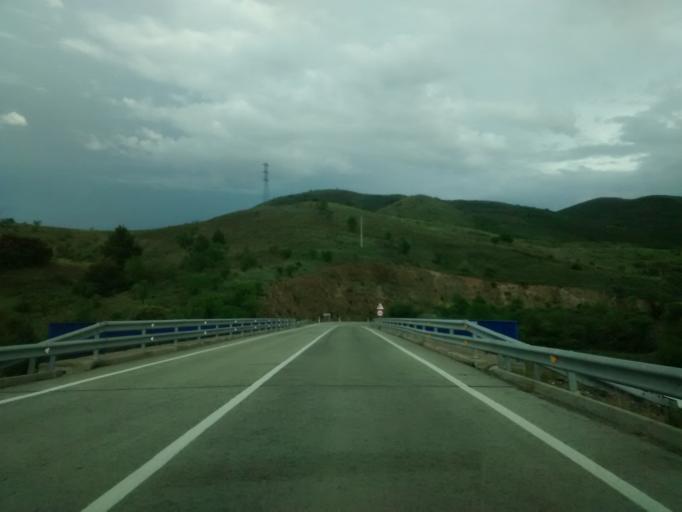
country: ES
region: Aragon
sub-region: Provincia de Zaragoza
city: Ateca
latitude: 41.3209
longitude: -1.7939
